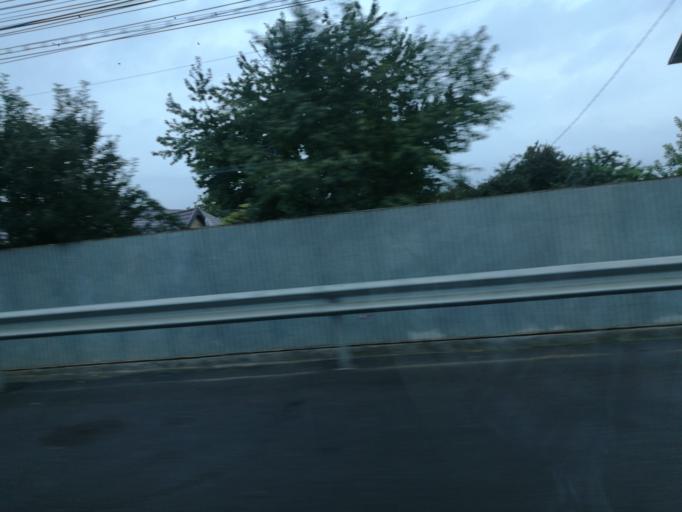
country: RO
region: Galati
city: Galati
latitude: 45.4676
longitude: 28.0346
